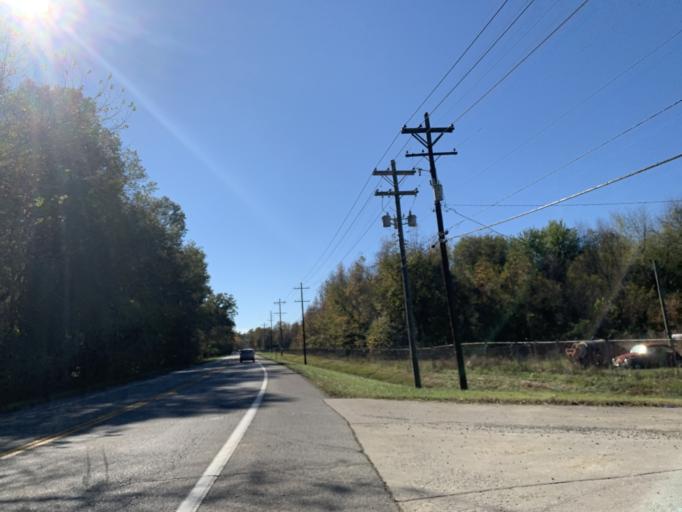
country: US
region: Kentucky
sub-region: Jefferson County
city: Saint Dennis
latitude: 38.1978
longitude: -85.8616
